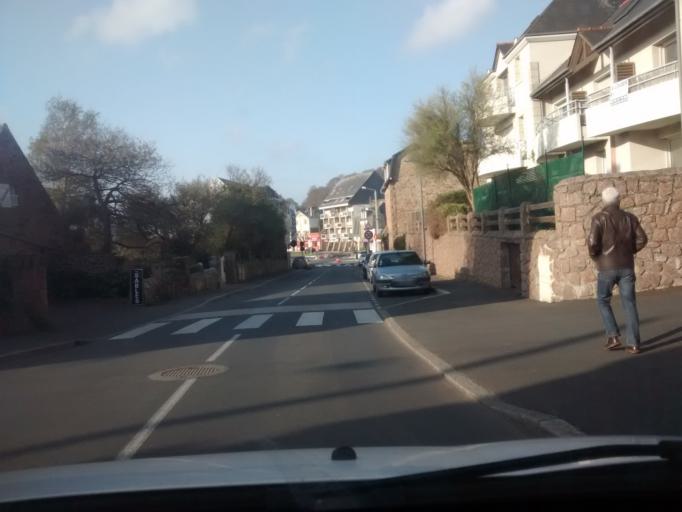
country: FR
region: Brittany
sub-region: Departement des Cotes-d'Armor
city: Perros-Guirec
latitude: 48.8087
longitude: -3.4408
